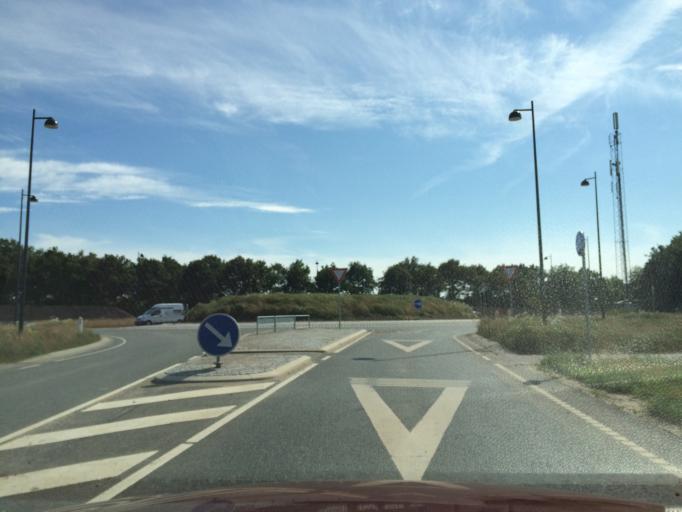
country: DK
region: Central Jutland
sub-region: Silkeborg Kommune
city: Silkeborg
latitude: 56.1979
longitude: 9.5466
